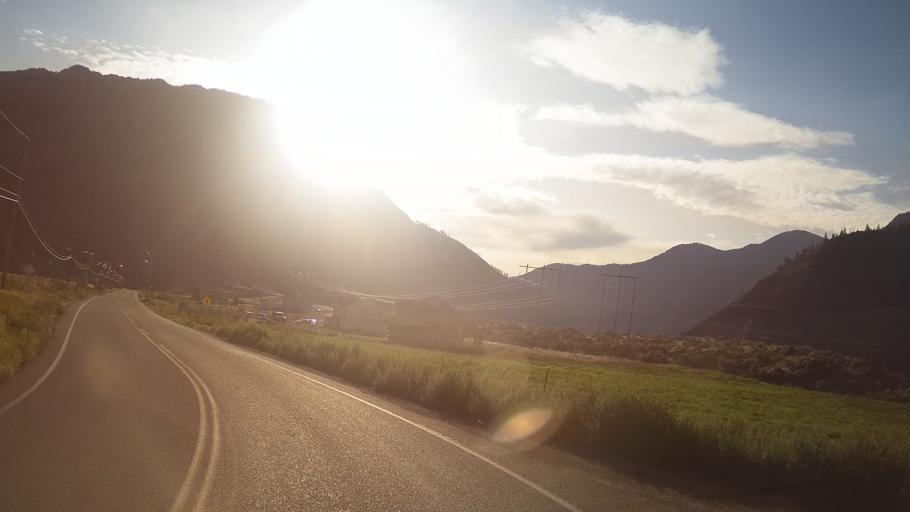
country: CA
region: British Columbia
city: Lillooet
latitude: 50.7424
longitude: -121.8621
